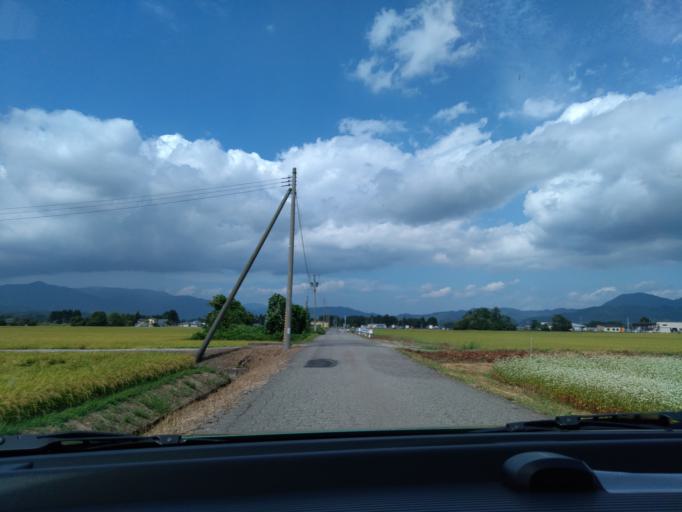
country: JP
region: Akita
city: Kakunodatemachi
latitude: 39.6088
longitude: 140.5845
